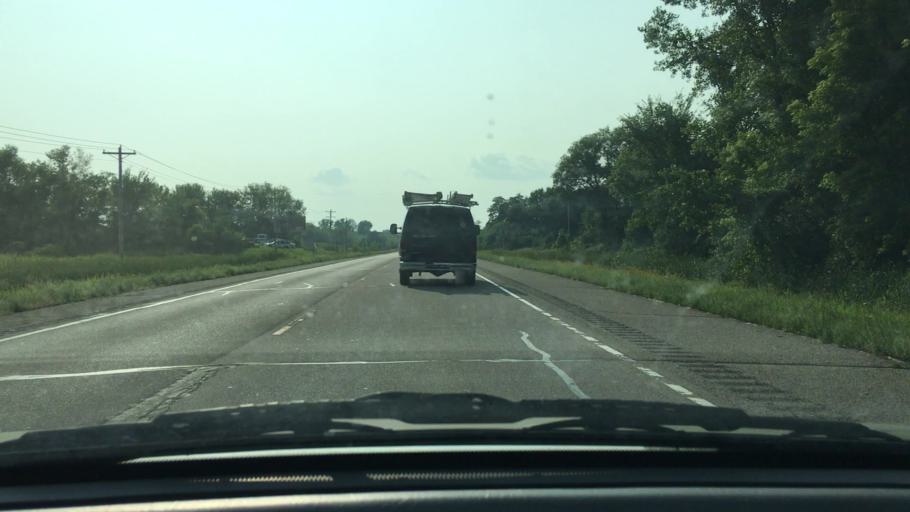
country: US
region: Minnesota
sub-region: Le Sueur County
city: New Prague
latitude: 44.5437
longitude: -93.5105
